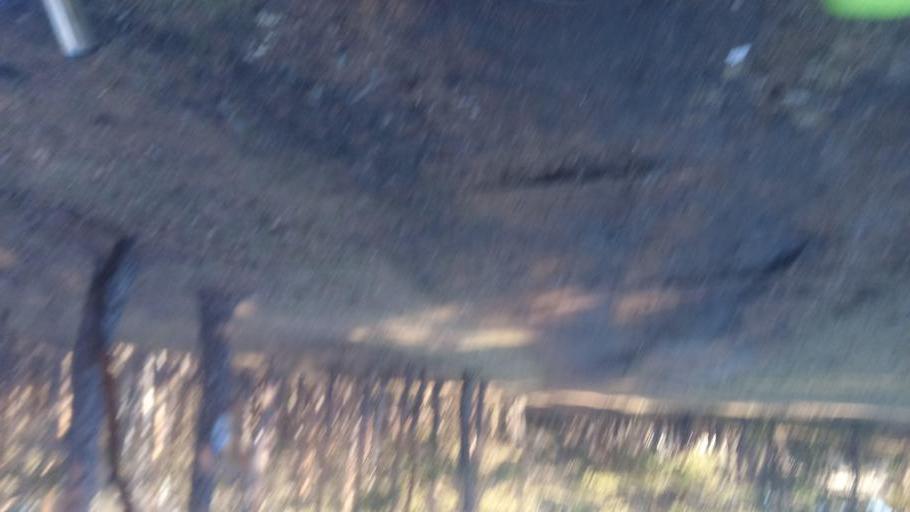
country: RU
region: Chelyabinsk
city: Novosineglazovskiy
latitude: 55.1261
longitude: 61.3324
